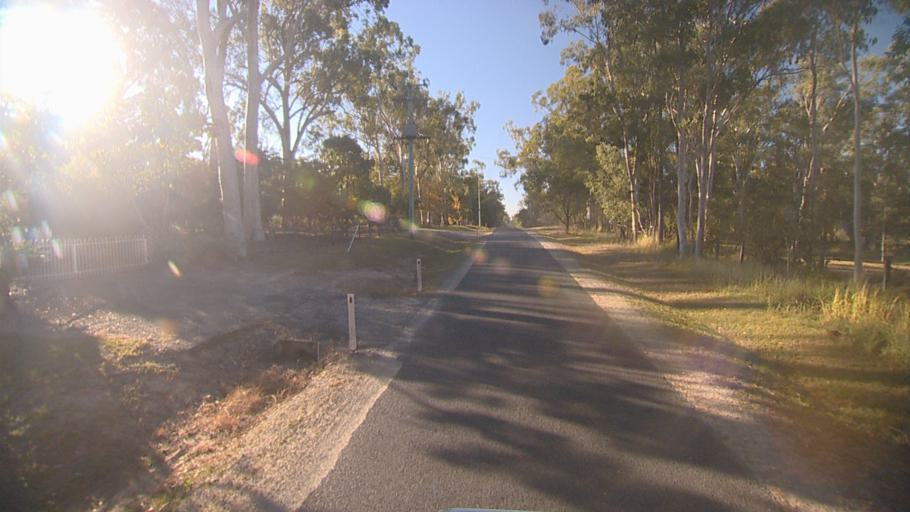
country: AU
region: Queensland
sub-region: Logan
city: Chambers Flat
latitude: -27.7880
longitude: 153.0859
